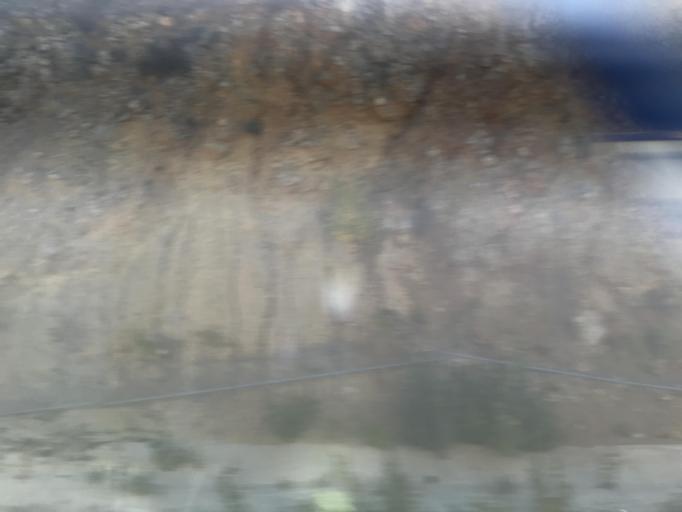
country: ES
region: Castille-La Mancha
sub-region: Provincia de Guadalajara
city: Anguita
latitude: 41.0866
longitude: -2.4041
